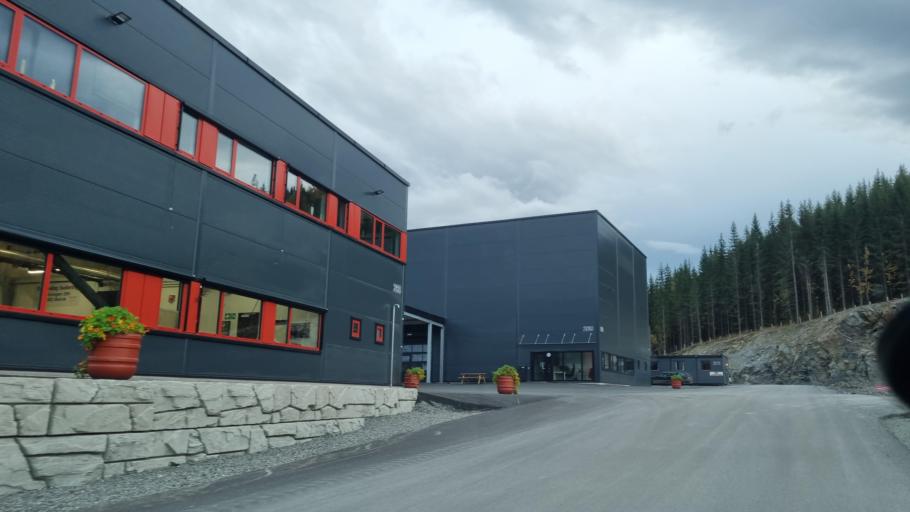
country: NO
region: Sor-Trondelag
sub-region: Malvik
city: Malvik
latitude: 63.4211
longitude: 10.7263
